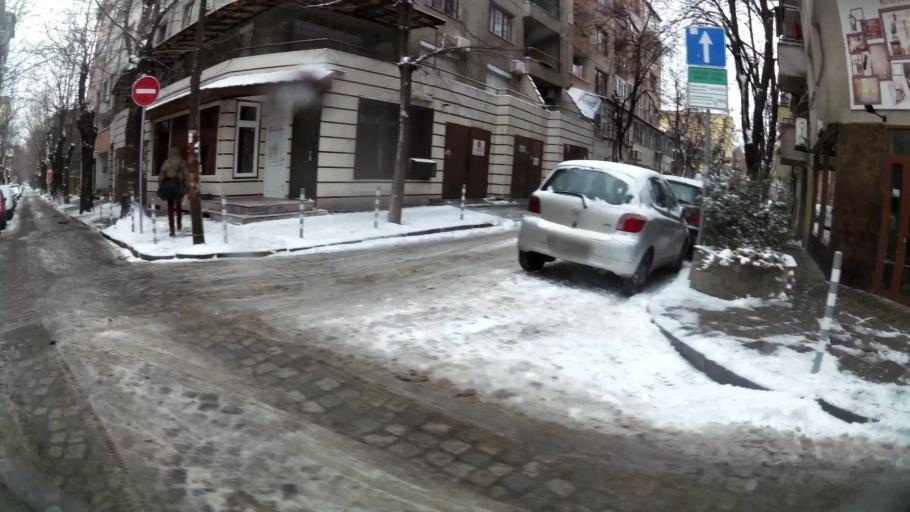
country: BG
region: Sofia-Capital
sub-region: Stolichna Obshtina
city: Sofia
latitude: 42.6957
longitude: 23.3496
